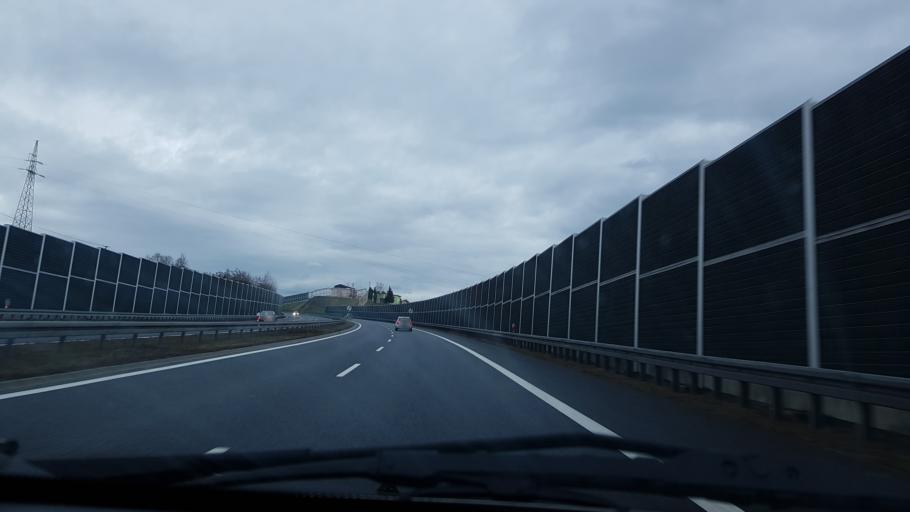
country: PL
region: Silesian Voivodeship
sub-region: Powiat cieszynski
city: Zamarski
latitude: 49.7625
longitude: 18.6741
